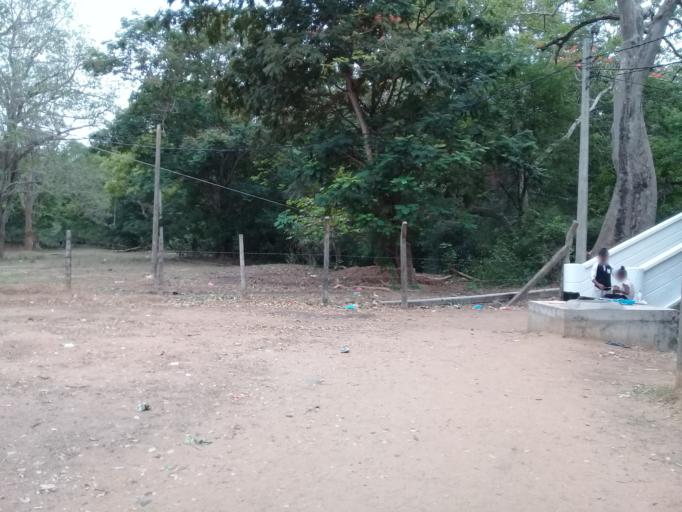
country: LK
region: Uva
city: Wattegama
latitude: 6.4153
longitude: 81.3355
